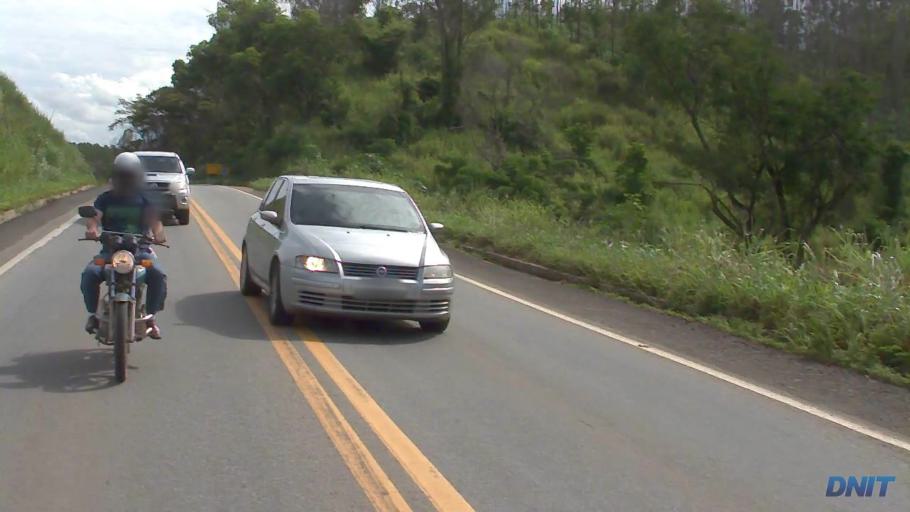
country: BR
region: Minas Gerais
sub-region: Ipaba
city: Ipaba
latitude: -19.3413
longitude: -42.4301
